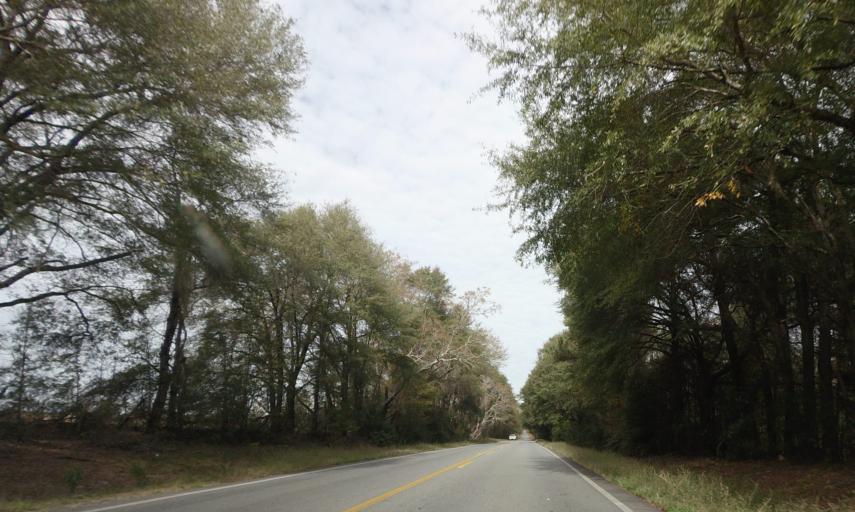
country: US
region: Georgia
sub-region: Dodge County
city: Chester
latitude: 32.4991
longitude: -83.0915
